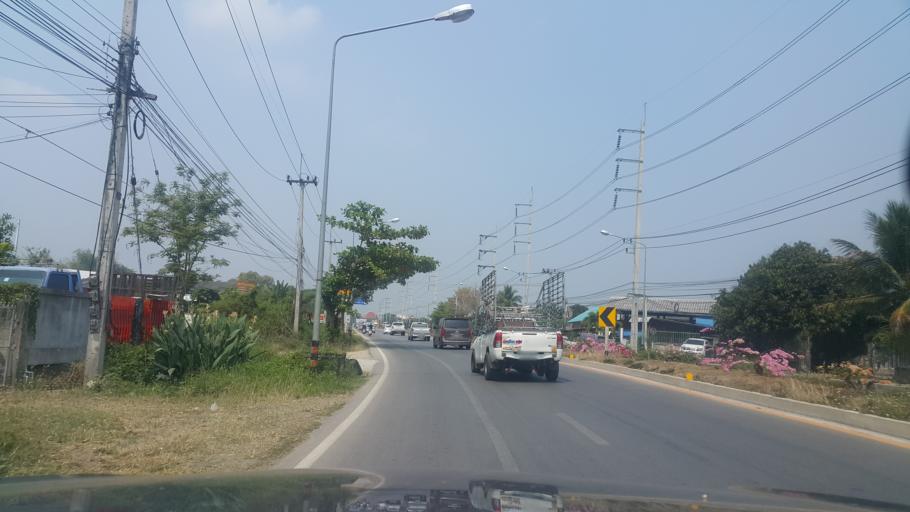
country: TH
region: Lamphun
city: Pa Sang
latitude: 18.4831
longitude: 98.9438
